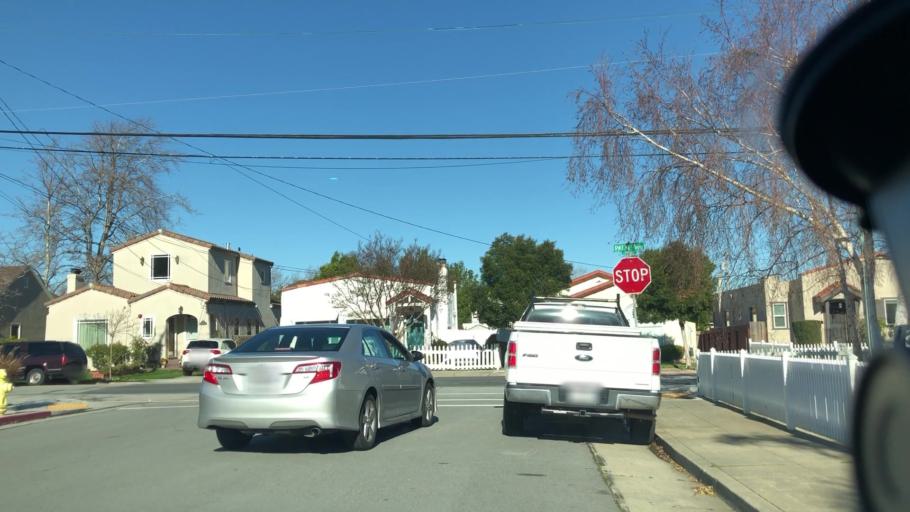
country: US
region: California
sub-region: San Mateo County
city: San Mateo
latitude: 37.5518
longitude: -122.3117
